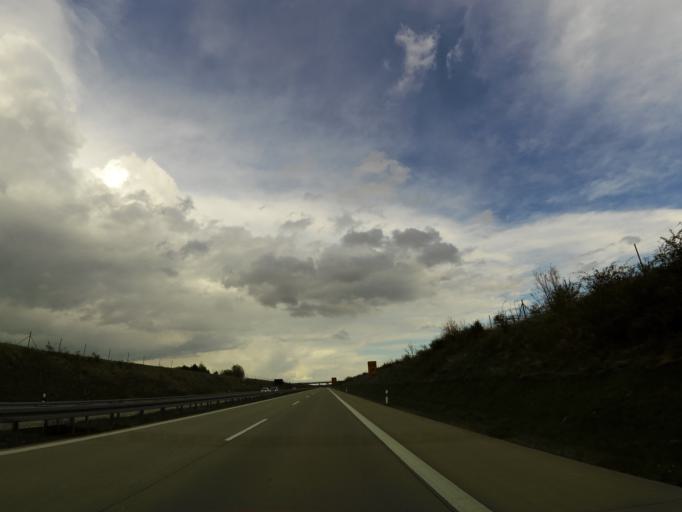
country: DE
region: Saxony-Anhalt
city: Blankenburg
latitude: 51.8049
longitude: 10.9798
